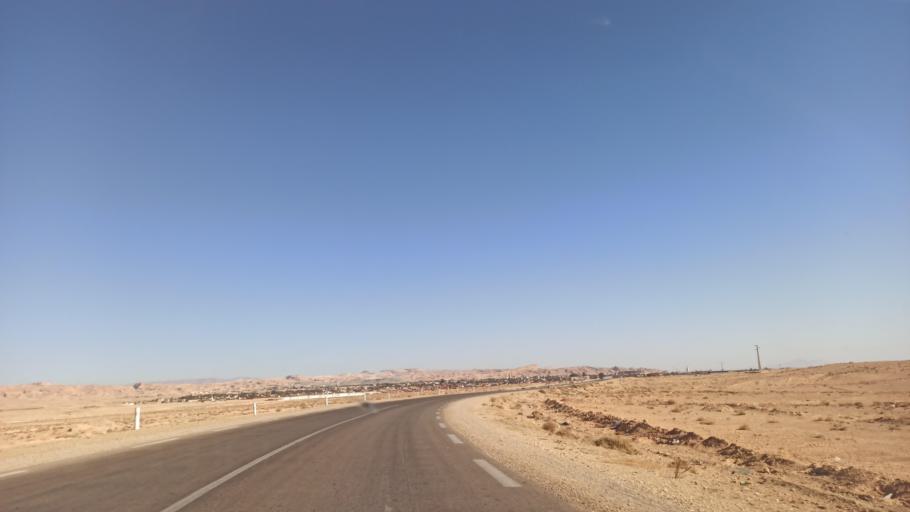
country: TN
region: Gafsa
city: Al Metlaoui
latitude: 34.3053
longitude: 8.3641
